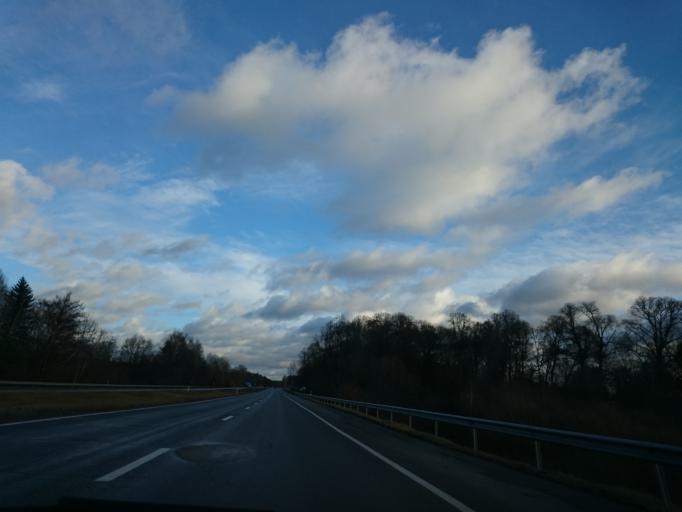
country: LV
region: Incukalns
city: Incukalns
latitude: 57.1234
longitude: 24.6807
